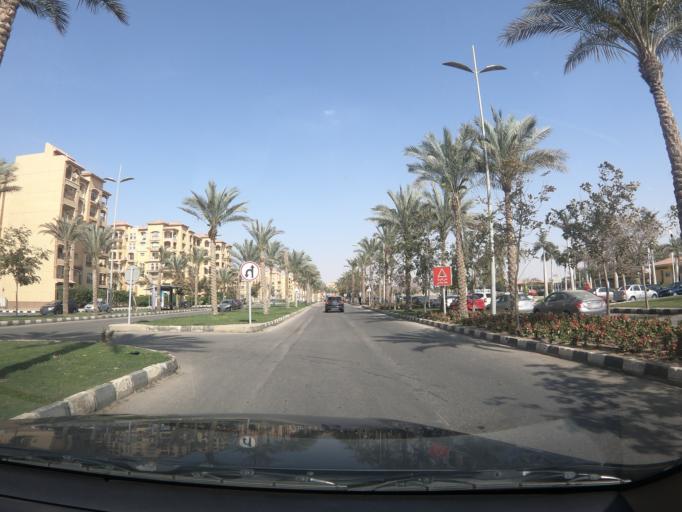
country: EG
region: Muhafazat al Qalyubiyah
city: Al Khankah
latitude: 30.0969
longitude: 31.6407
